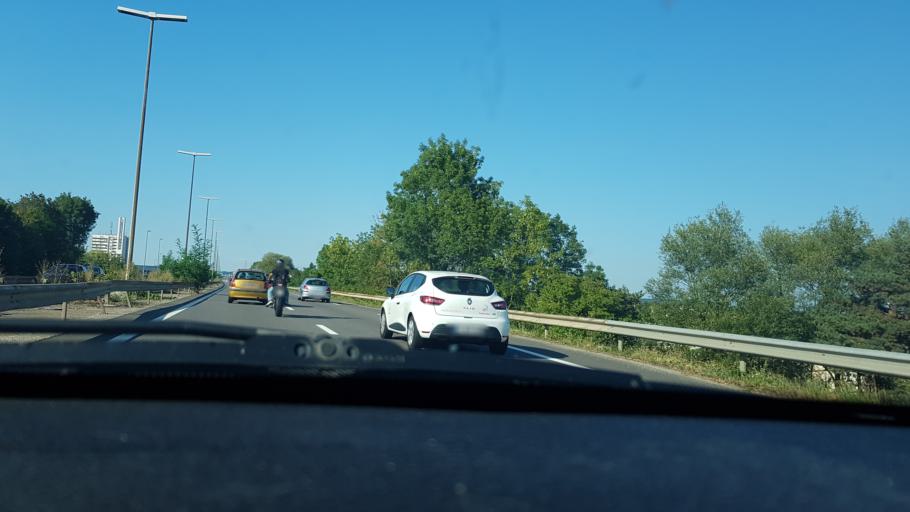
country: FR
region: Lorraine
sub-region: Departement de Meurthe-et-Moselle
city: Vandoeuvre-les-Nancy
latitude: 48.6549
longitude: 6.1837
